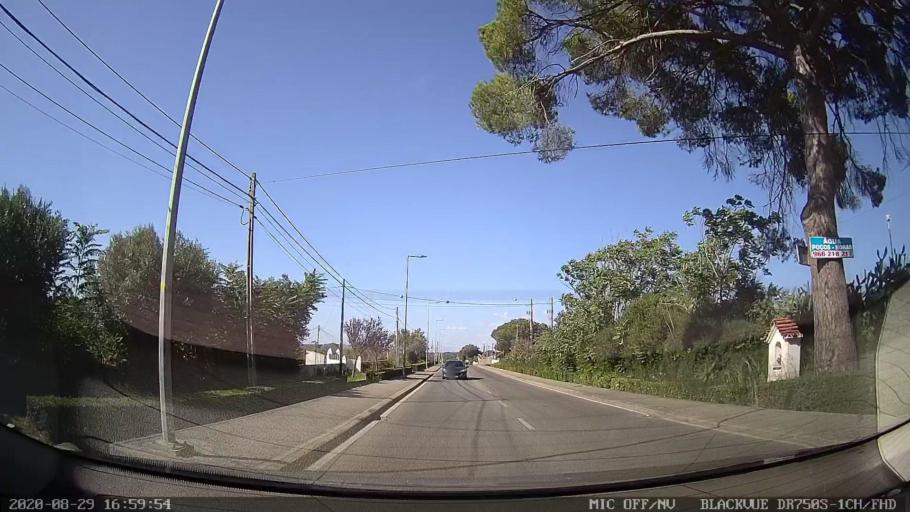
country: PT
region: Setubal
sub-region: Alcacer do Sal
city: Alcacer do Sal
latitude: 38.3832
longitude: -8.5134
